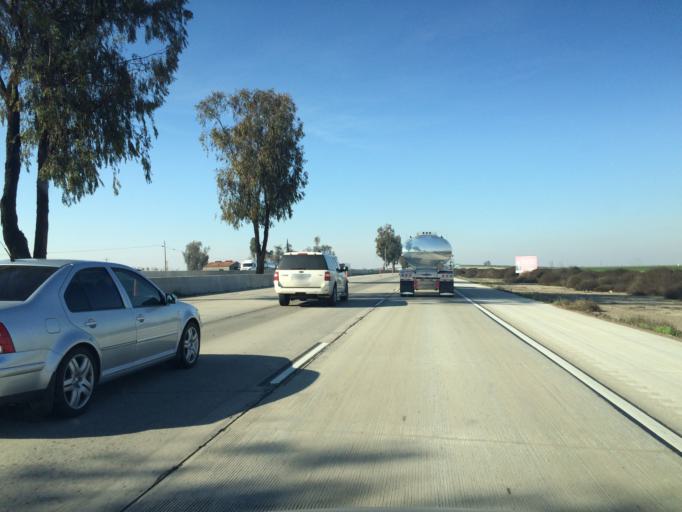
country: US
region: California
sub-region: Tulare County
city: Goshen
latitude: 36.3765
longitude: -119.4379
